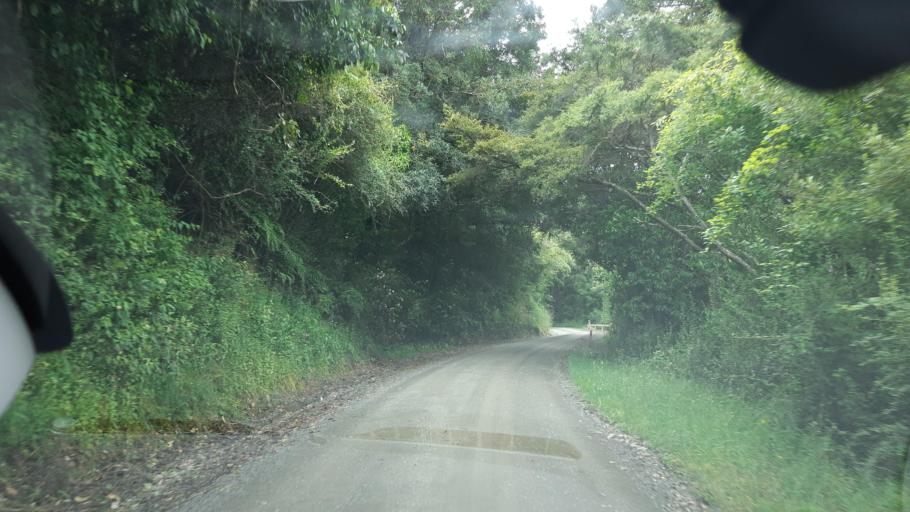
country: NZ
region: Tasman
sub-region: Tasman District
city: Wakefield
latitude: -41.4509
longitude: 173.0869
